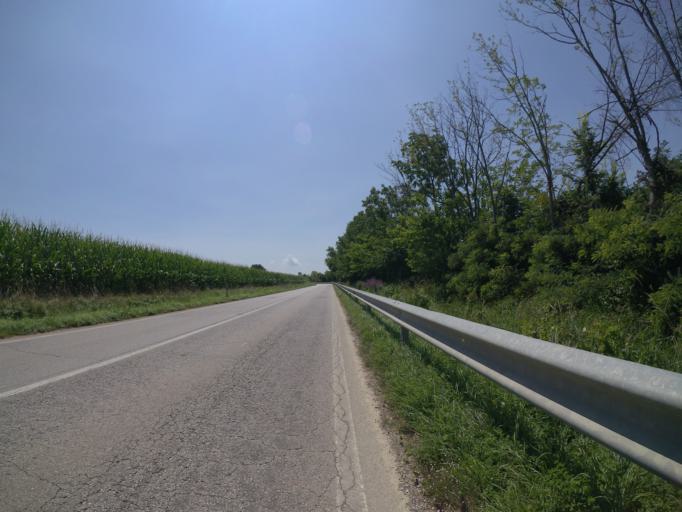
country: IT
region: Friuli Venezia Giulia
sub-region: Provincia di Udine
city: Lestizza
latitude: 45.9639
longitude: 13.1404
